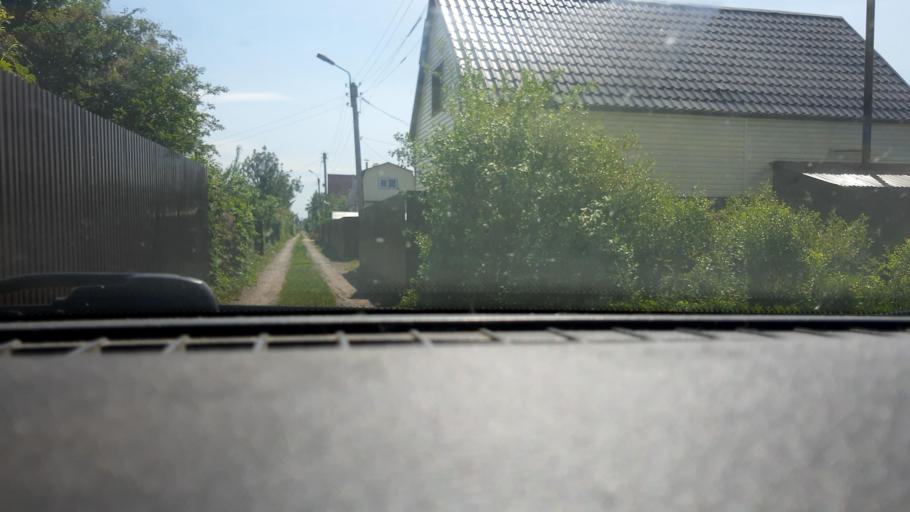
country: RU
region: Bashkortostan
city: Mikhaylovka
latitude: 54.7954
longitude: 55.8242
